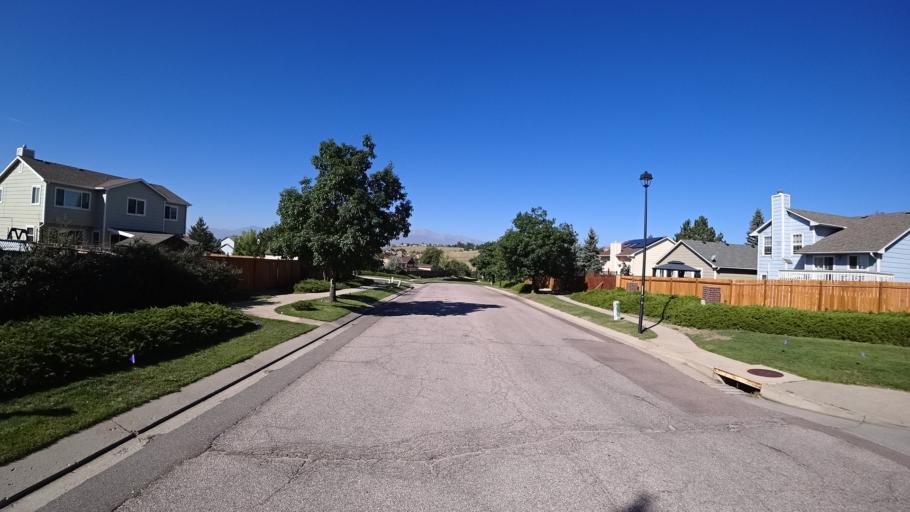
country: US
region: Colorado
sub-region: El Paso County
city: Black Forest
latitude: 38.9492
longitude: -104.7400
